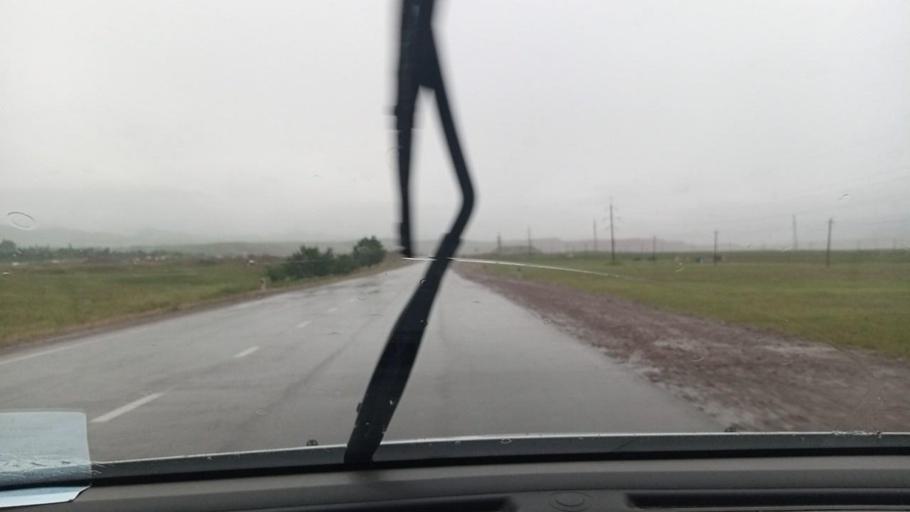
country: UZ
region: Toshkent
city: Angren
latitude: 41.0398
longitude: 70.1500
